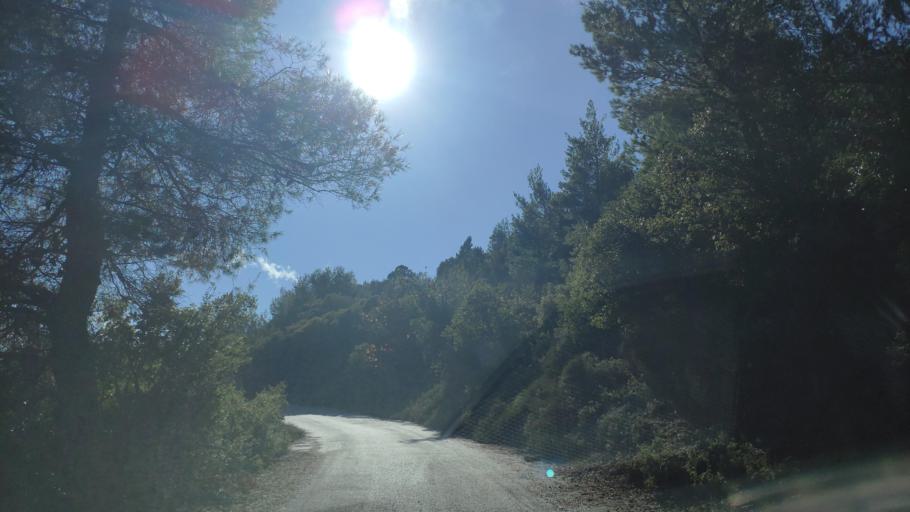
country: GR
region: West Greece
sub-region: Nomos Achaias
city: Aiyira
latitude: 38.0614
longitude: 22.4568
